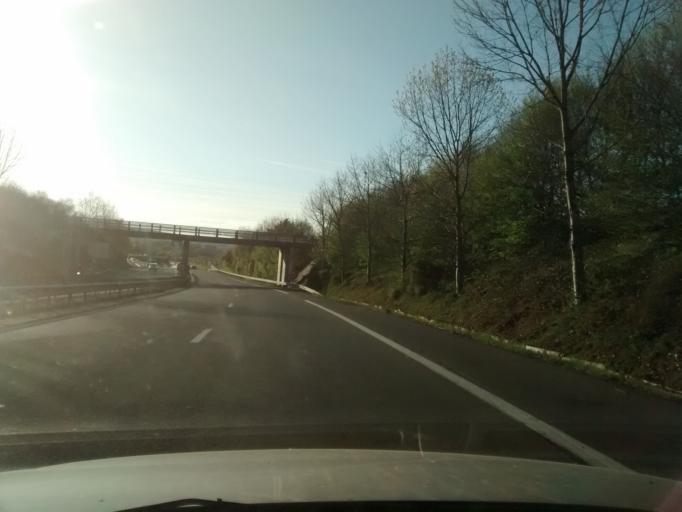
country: FR
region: Pays de la Loire
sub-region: Departement de la Sarthe
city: Coulaines
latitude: 48.0333
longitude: 0.2116
